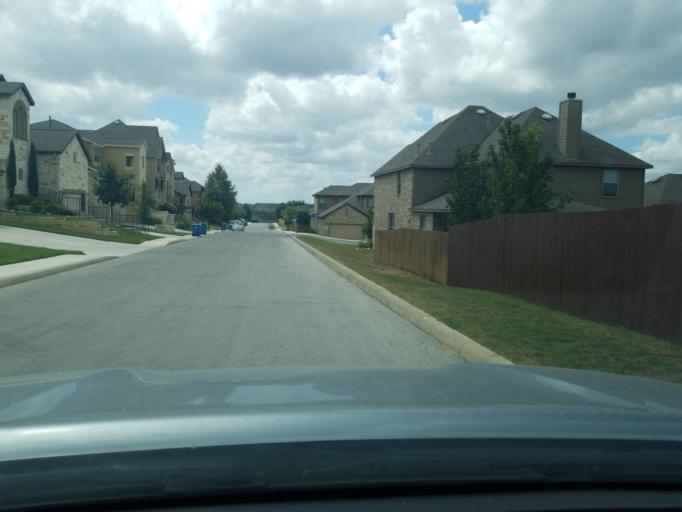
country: US
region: Texas
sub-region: Bexar County
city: Timberwood Park
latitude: 29.6661
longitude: -98.5061
